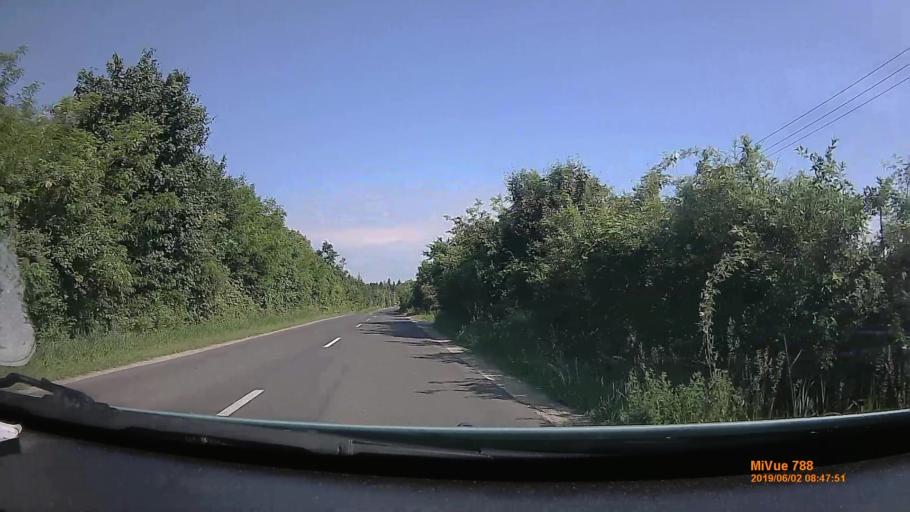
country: HU
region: Borsod-Abauj-Zemplen
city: Sajobabony
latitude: 48.1308
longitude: 20.7084
